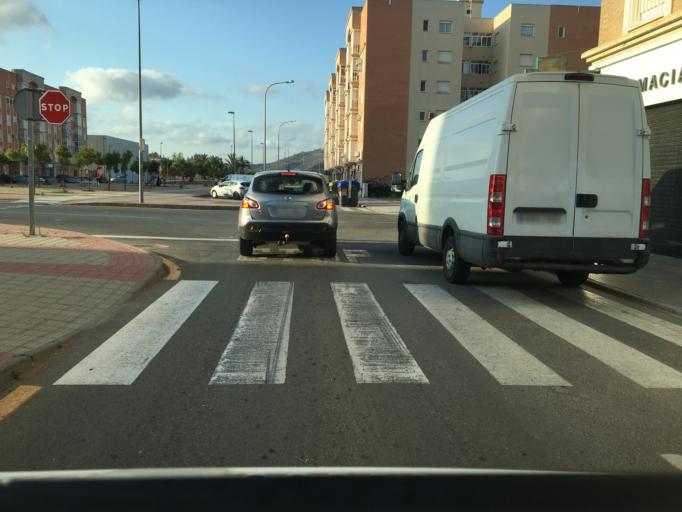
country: ES
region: Murcia
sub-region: Murcia
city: Cartagena
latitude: 37.6214
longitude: -1.0050
